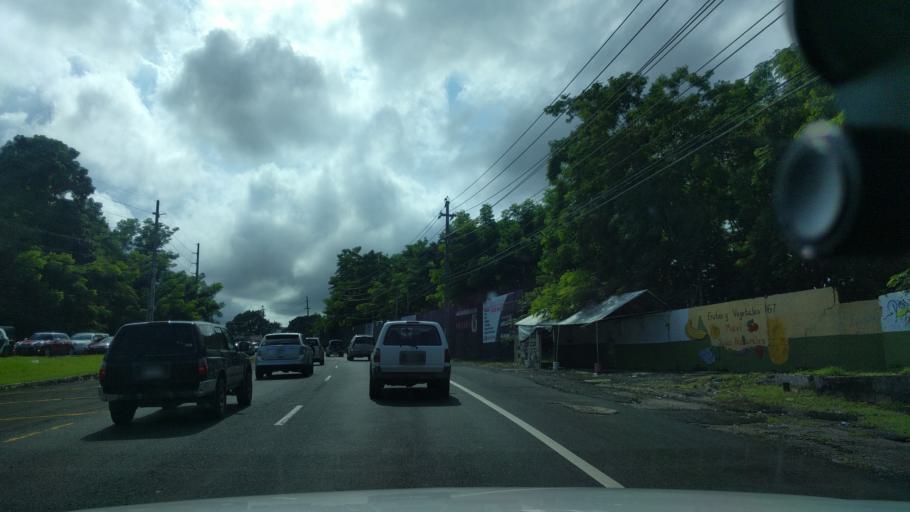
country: PR
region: Toa Alta
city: Pajaros
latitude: 18.3608
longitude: -66.1900
